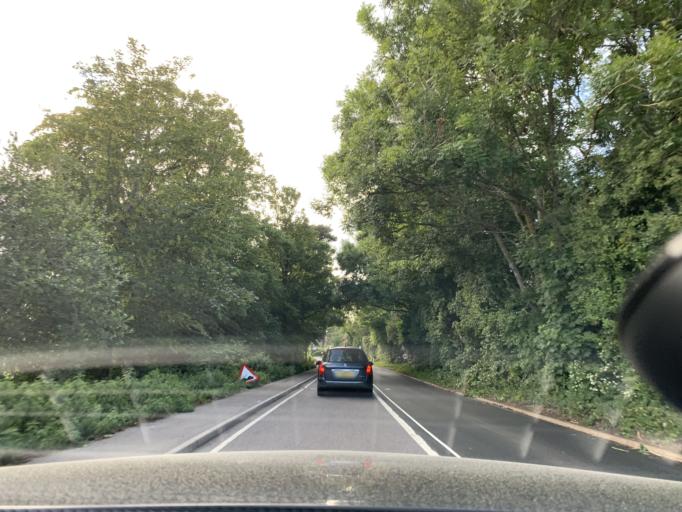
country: GB
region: England
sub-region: East Sussex
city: Robertsbridge
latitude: 50.9553
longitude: 0.4993
